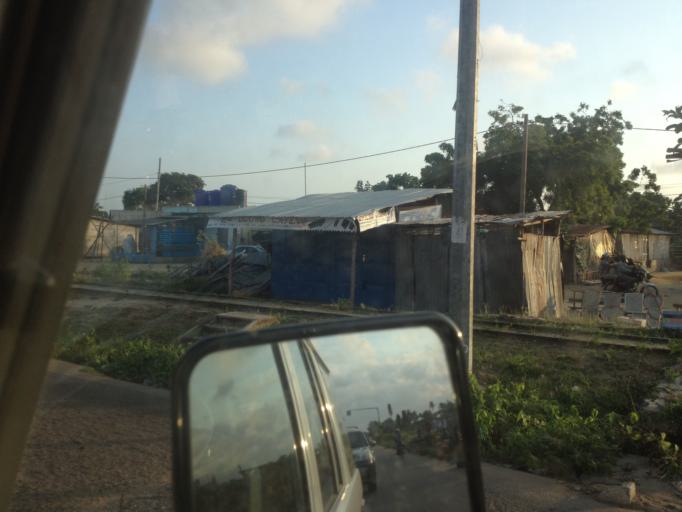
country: BJ
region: Queme
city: Porto-Novo
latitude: 6.4264
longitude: 2.6273
